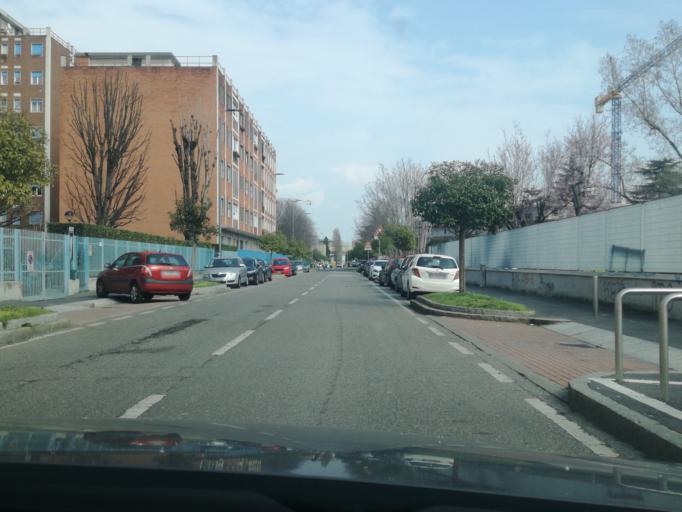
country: IT
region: Lombardy
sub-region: Citta metropolitana di Milano
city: Milano
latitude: 45.4360
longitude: 9.1613
